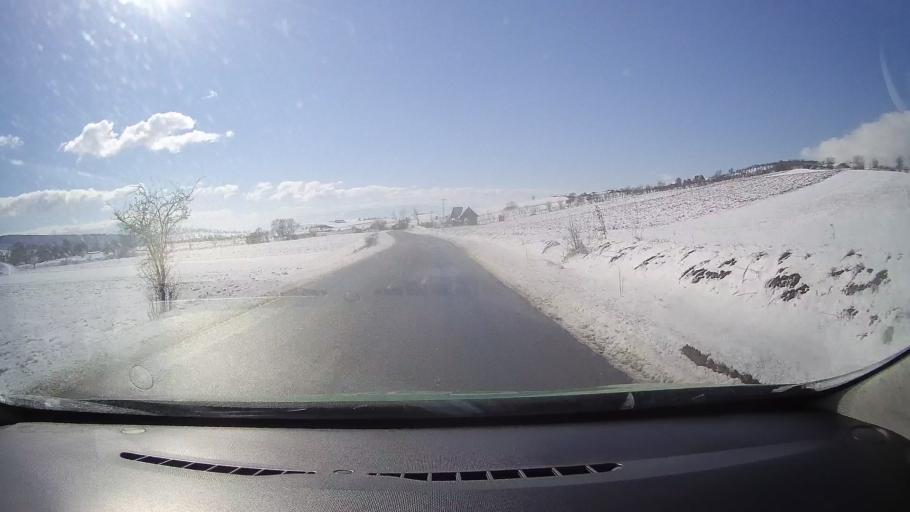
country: RO
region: Sibiu
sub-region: Comuna Vurpar
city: Vurpar
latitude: 45.8776
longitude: 24.3213
